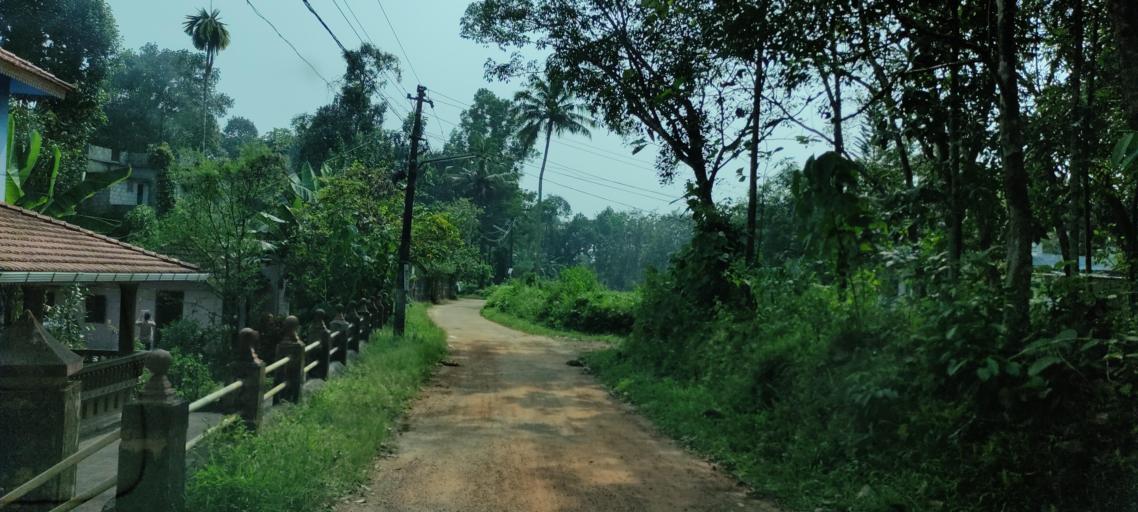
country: IN
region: Kerala
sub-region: Pattanamtitta
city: Adur
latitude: 9.2043
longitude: 76.6938
